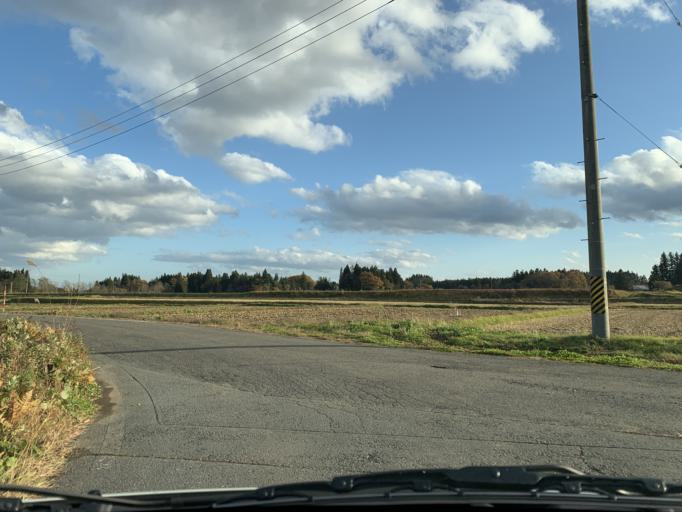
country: JP
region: Iwate
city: Mizusawa
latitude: 39.1195
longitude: 140.9944
